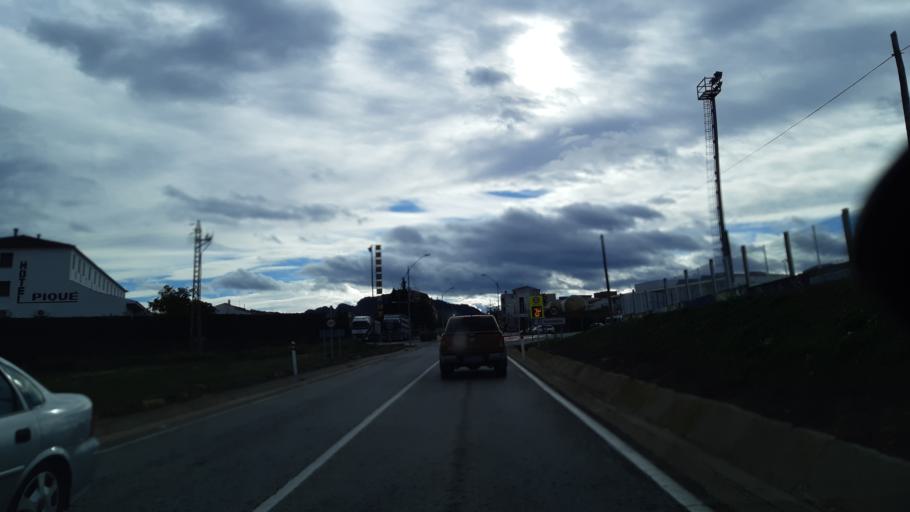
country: ES
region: Catalonia
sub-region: Provincia de Tarragona
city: Gandesa
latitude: 41.0591
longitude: 0.4418
